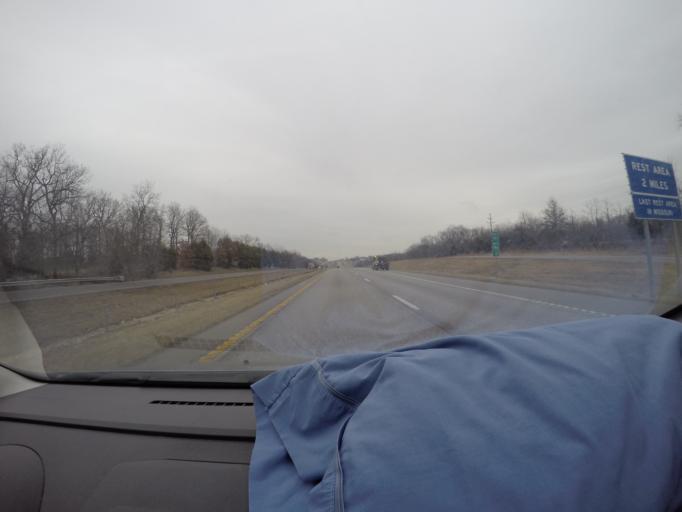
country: US
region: Missouri
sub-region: Warren County
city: Warrenton
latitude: 38.8204
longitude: -91.0953
